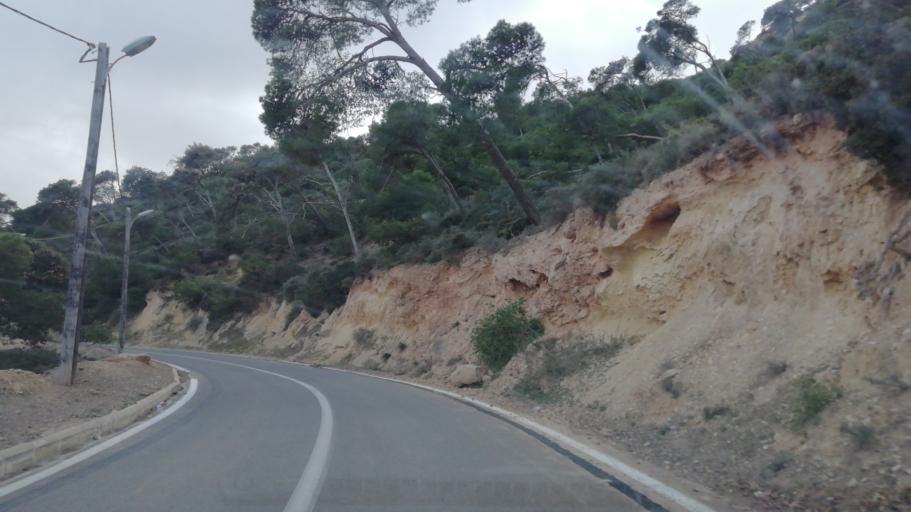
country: DZ
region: Oran
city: Oran
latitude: 35.7071
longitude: -0.6692
